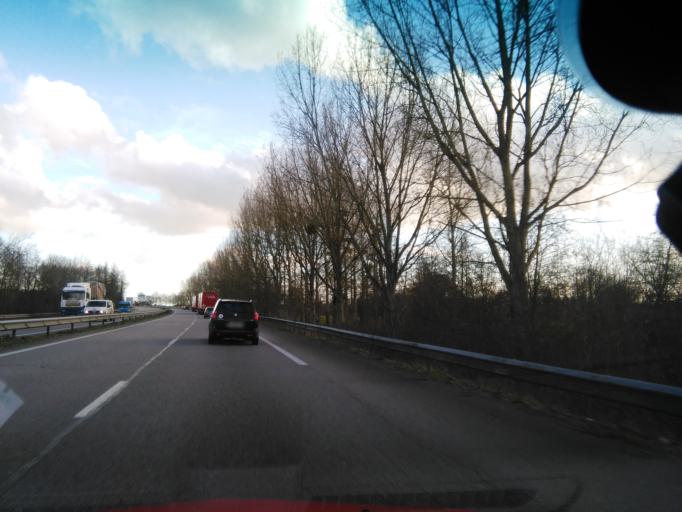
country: FR
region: Lower Normandy
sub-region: Departement du Calvados
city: Potigny
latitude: 48.9552
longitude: -0.2251
